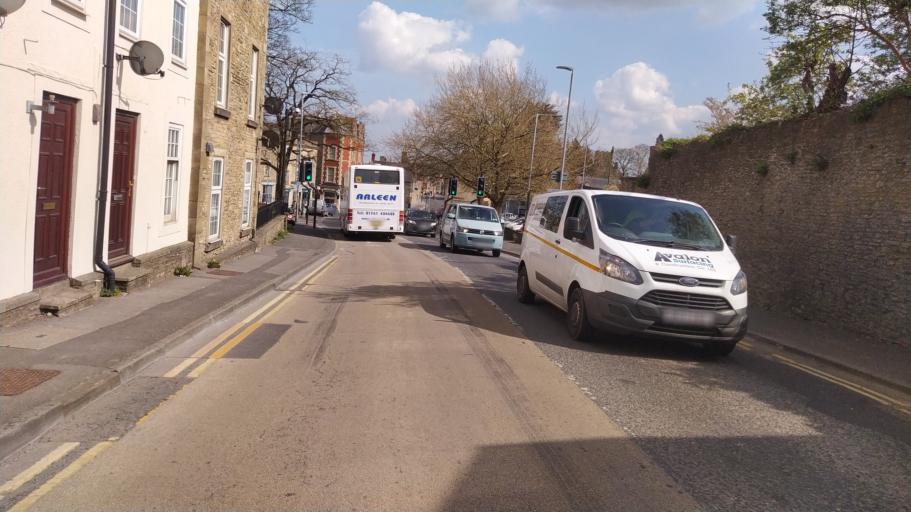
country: GB
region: England
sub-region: Somerset
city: Frome
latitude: 51.2311
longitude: -2.3290
